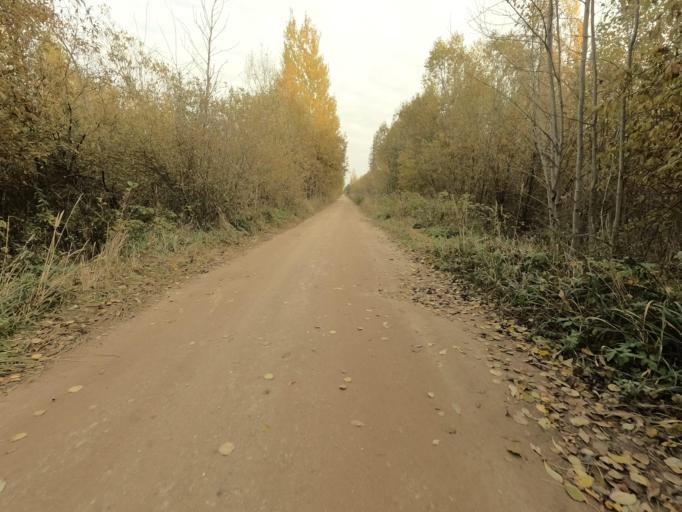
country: RU
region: Novgorod
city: Pankovka
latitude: 58.8975
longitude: 30.9981
